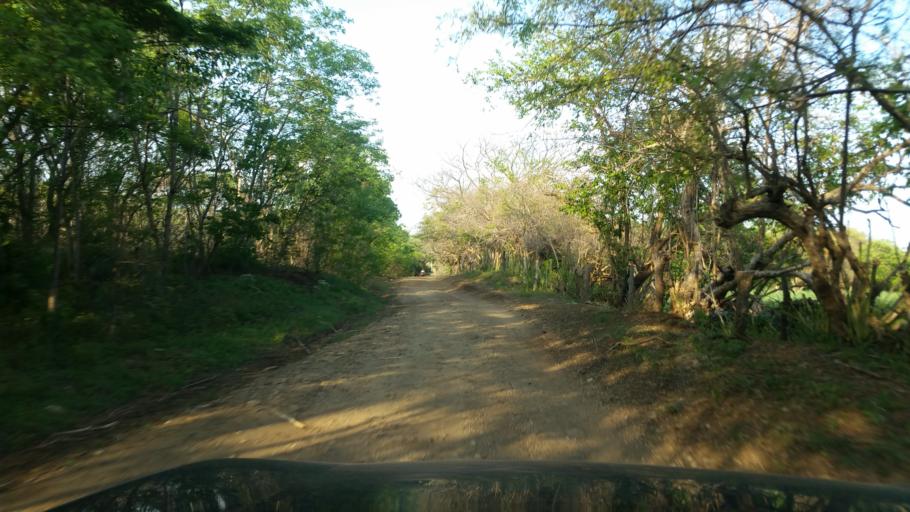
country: NI
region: Managua
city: Masachapa
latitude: 11.7767
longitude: -86.4800
